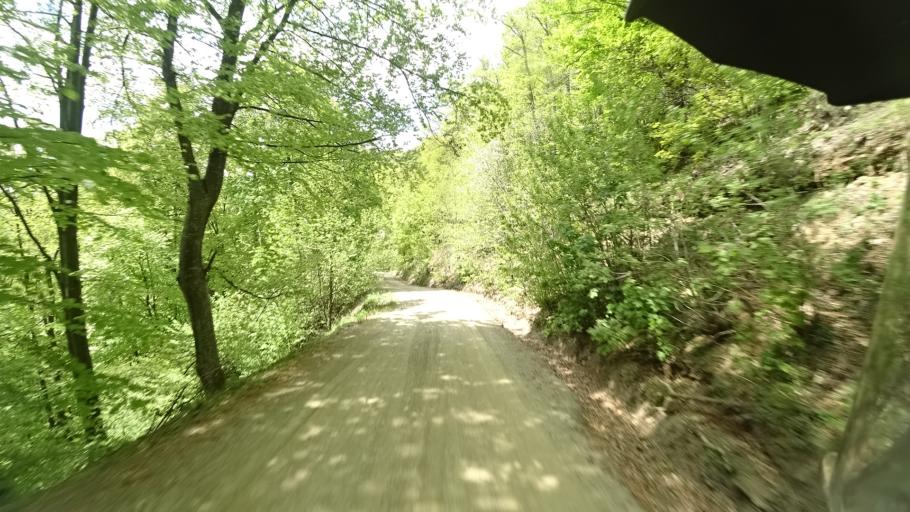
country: HR
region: Grad Zagreb
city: Kasina
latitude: 45.9102
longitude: 15.9969
